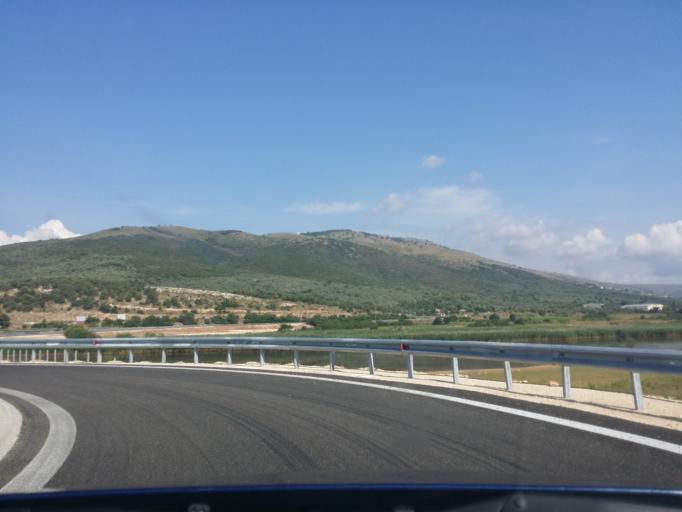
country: GR
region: West Greece
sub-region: Nomos Aitolias kai Akarnanias
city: Stanos
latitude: 38.7783
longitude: 21.1910
